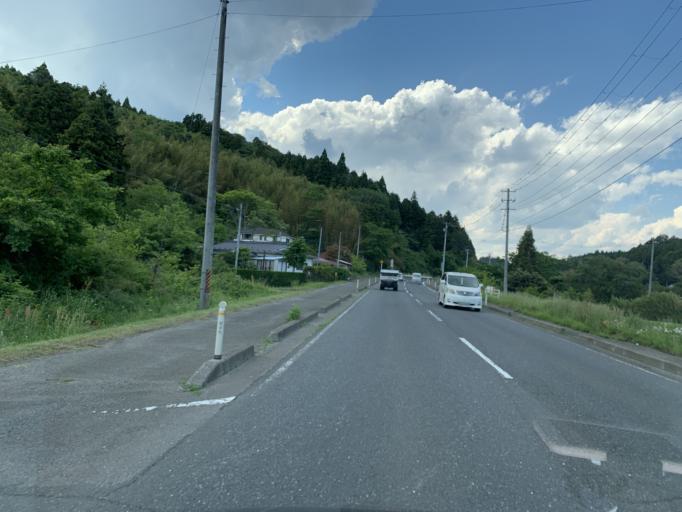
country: JP
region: Miyagi
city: Wakuya
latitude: 38.5510
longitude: 141.1406
